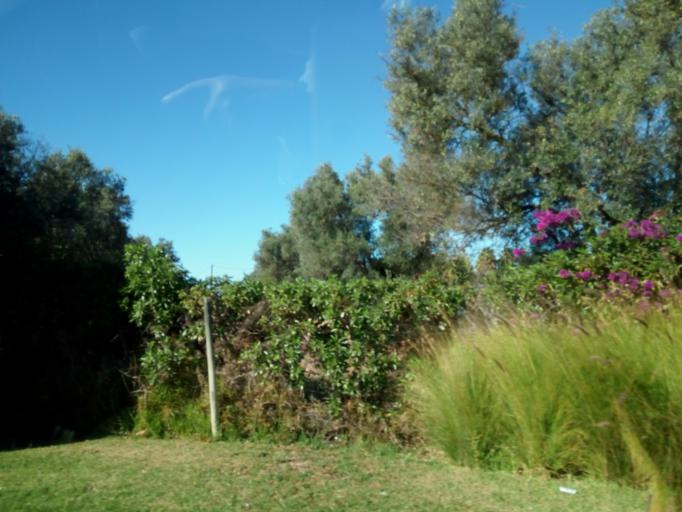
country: PT
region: Faro
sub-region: Loule
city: Vilamoura
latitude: 37.1119
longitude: -8.1194
